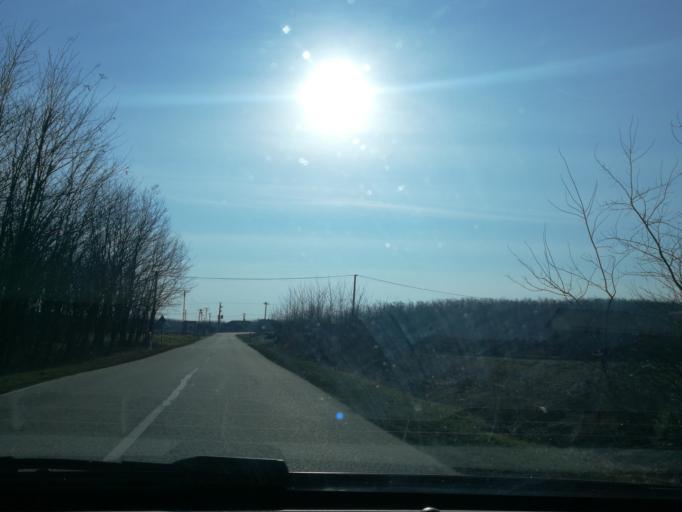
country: HU
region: Szabolcs-Szatmar-Bereg
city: Demecser
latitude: 48.0487
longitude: 21.9693
